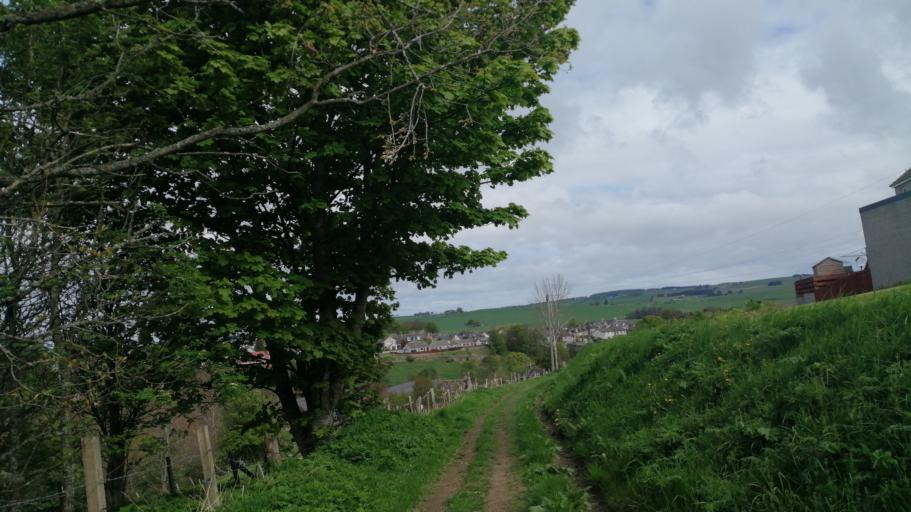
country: GB
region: Scotland
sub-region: Moray
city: Keith
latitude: 57.5386
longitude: -2.9588
